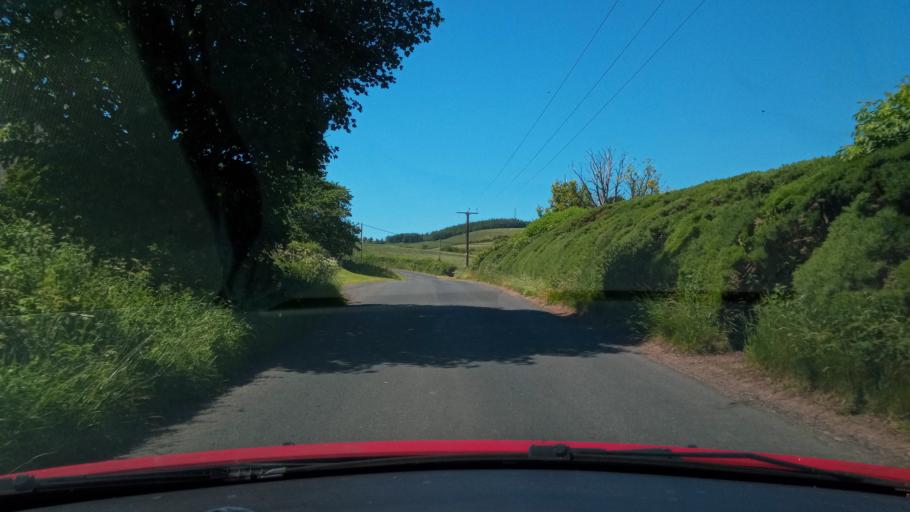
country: GB
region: Scotland
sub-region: The Scottish Borders
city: Duns
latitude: 55.7785
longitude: -2.3933
